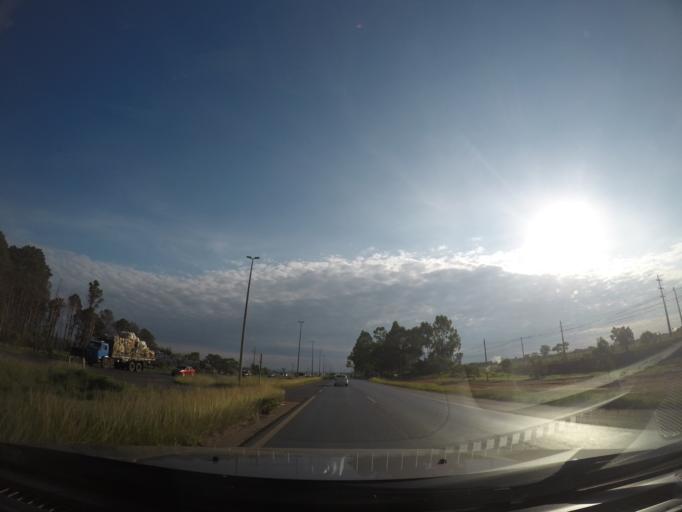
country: BR
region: Federal District
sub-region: Brasilia
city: Brasilia
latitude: -15.6386
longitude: -47.7489
